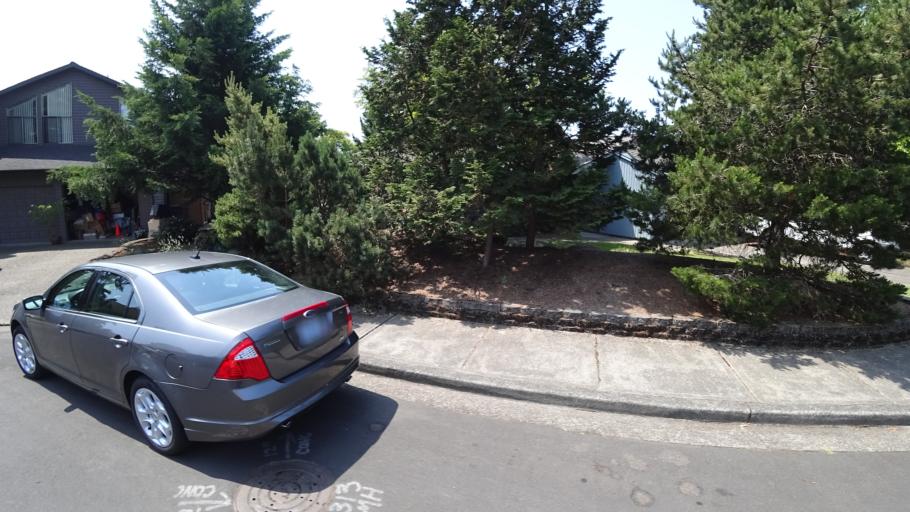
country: US
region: Oregon
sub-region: Washington County
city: Oak Hills
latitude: 45.5352
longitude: -122.8359
